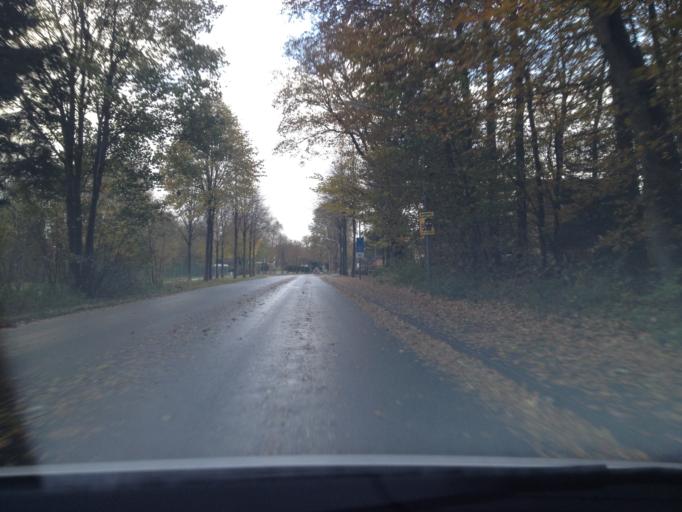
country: DE
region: Schleswig-Holstein
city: Leck
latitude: 54.7790
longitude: 8.9607
